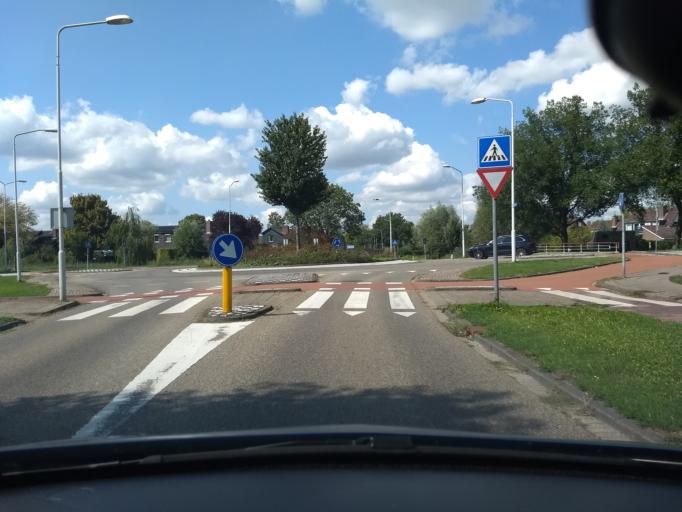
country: NL
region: South Holland
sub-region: Gemeente Papendrecht
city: Papendrecht
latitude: 51.8401
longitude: 4.6971
